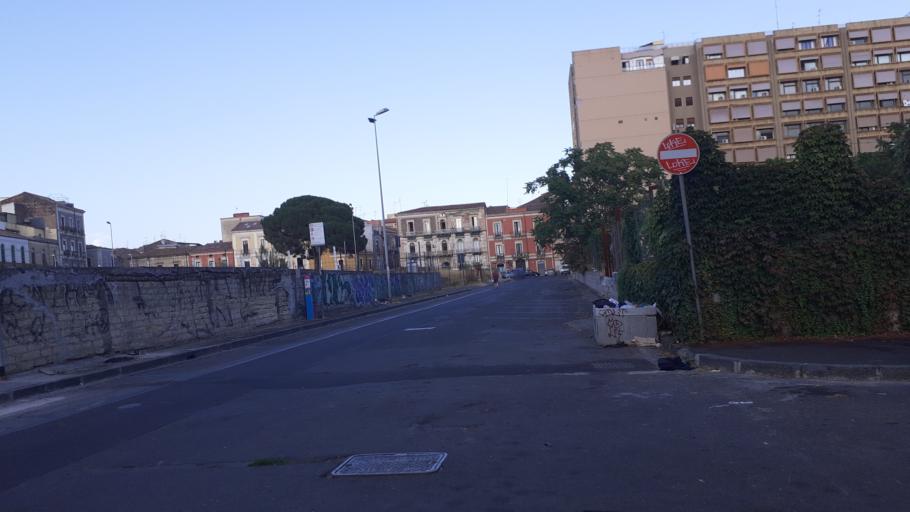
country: IT
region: Sicily
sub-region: Catania
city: Catania
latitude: 37.5084
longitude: 15.0910
